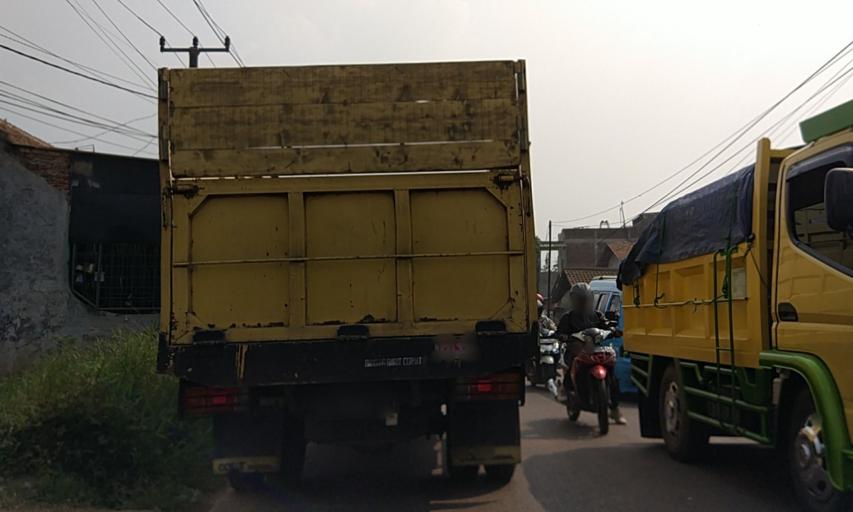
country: ID
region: West Java
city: Banjaran
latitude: -7.0467
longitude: 107.5788
